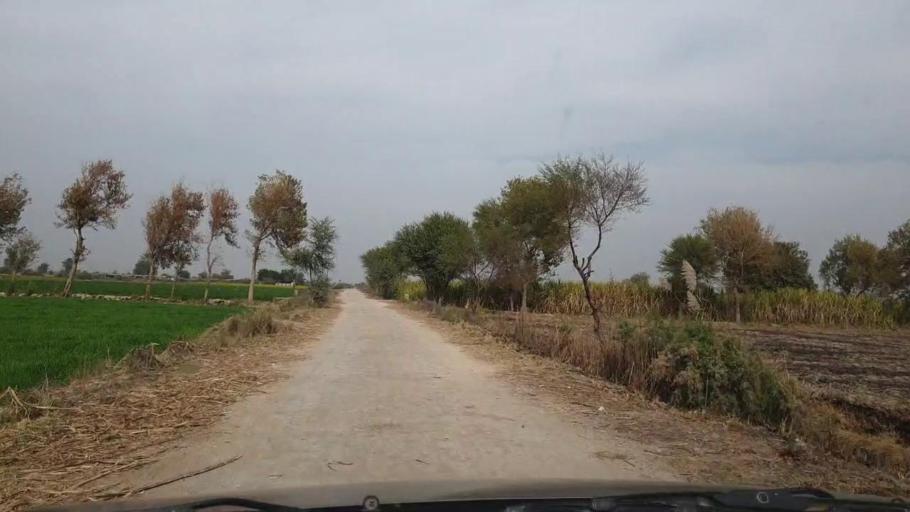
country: PK
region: Sindh
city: Sinjhoro
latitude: 26.0893
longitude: 68.8279
